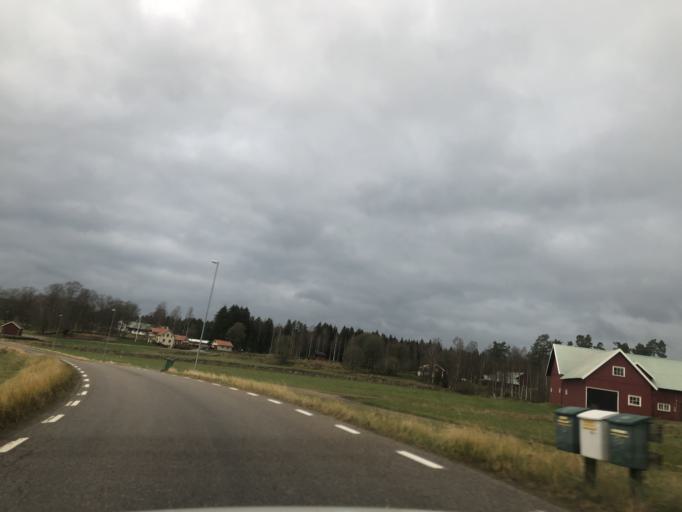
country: SE
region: Vaestra Goetaland
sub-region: Boras Kommun
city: Dalsjofors
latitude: 57.8287
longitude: 13.1758
